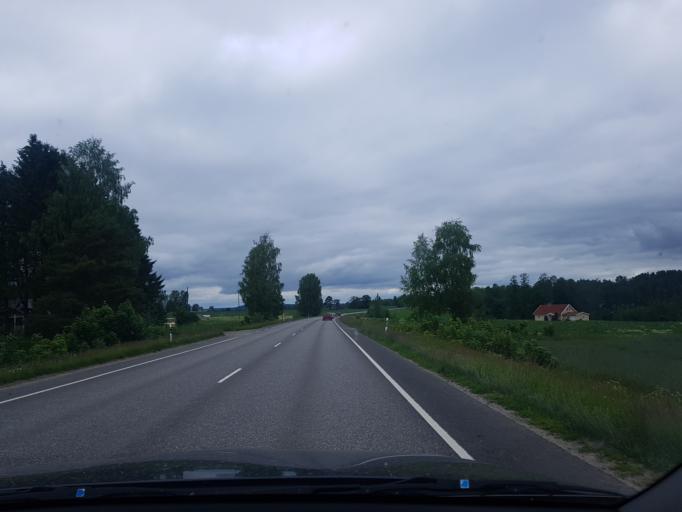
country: FI
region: Pirkanmaa
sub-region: Tampere
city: Paelkaene
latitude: 61.2522
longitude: 24.3525
